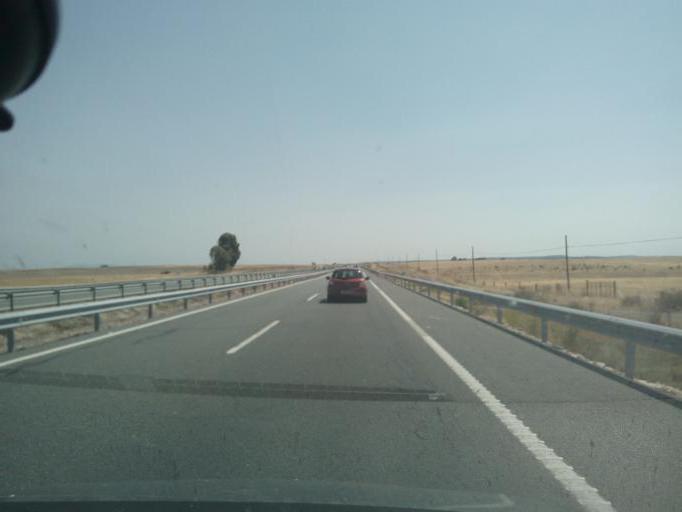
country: ES
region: Extremadura
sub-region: Provincia de Caceres
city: Peraleda de la Mata
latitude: 39.8920
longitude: -5.3909
